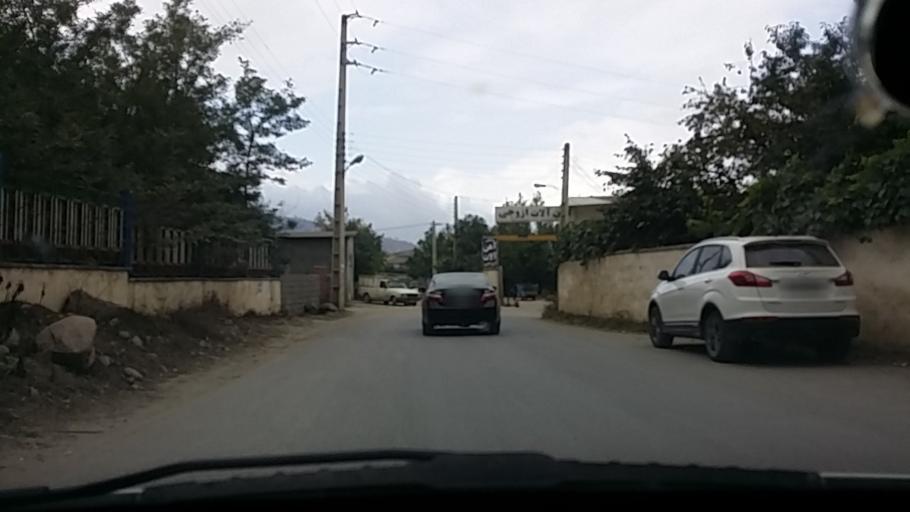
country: IR
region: Mazandaran
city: `Abbasabad
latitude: 36.5079
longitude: 51.1705
